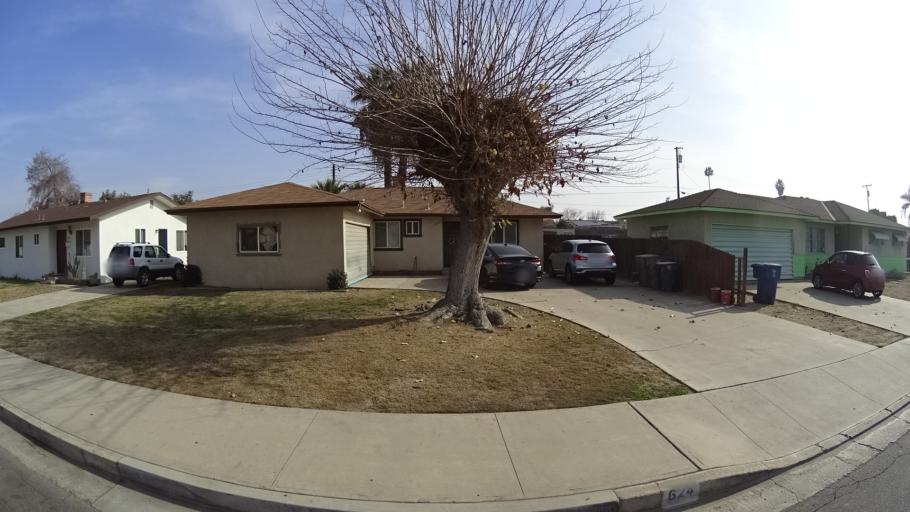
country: US
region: California
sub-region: Kern County
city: Bakersfield
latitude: 35.3478
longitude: -119.0163
